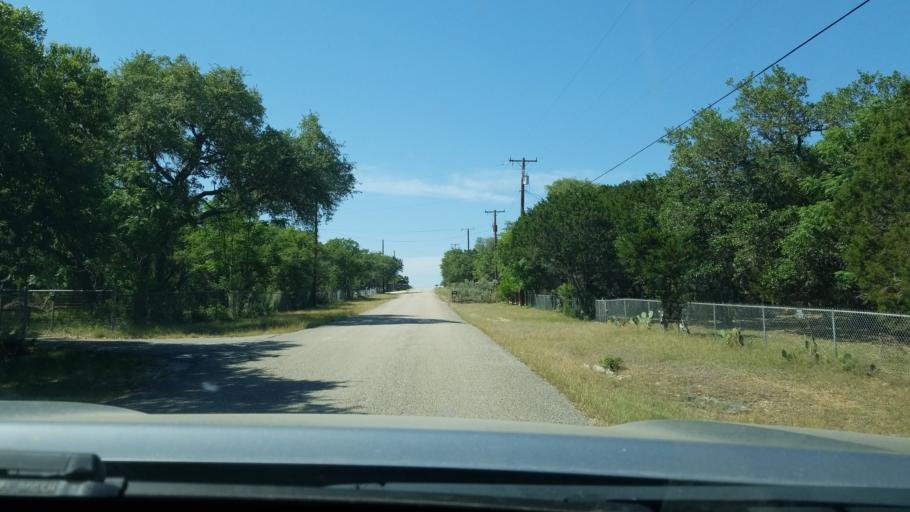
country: US
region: Texas
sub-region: Comal County
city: Bulverde
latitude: 29.7636
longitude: -98.5153
